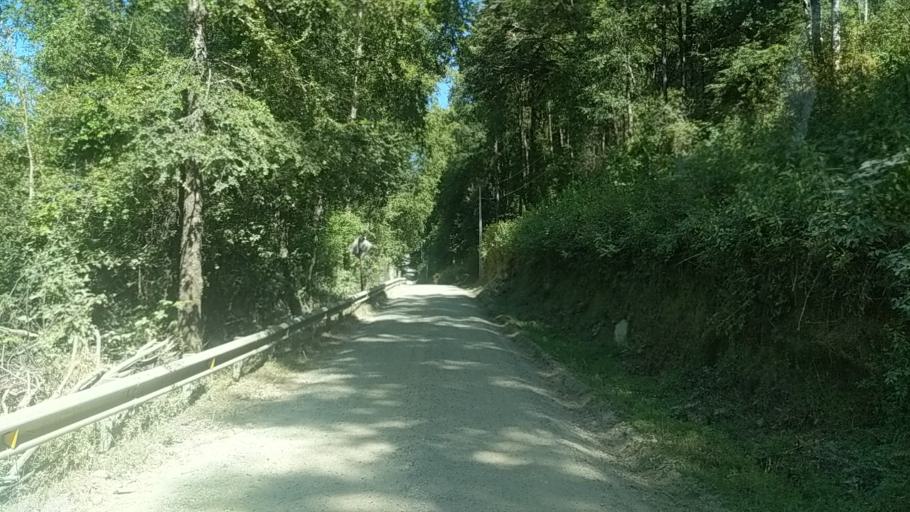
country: CL
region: Araucania
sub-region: Provincia de Cautin
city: Pucon
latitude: -39.0634
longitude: -71.7198
